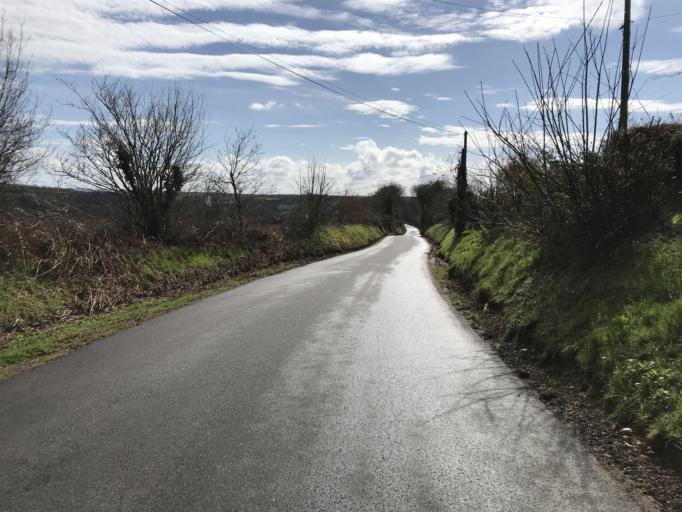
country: FR
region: Brittany
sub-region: Departement du Finistere
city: Daoulas
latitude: 48.3684
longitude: -4.2671
